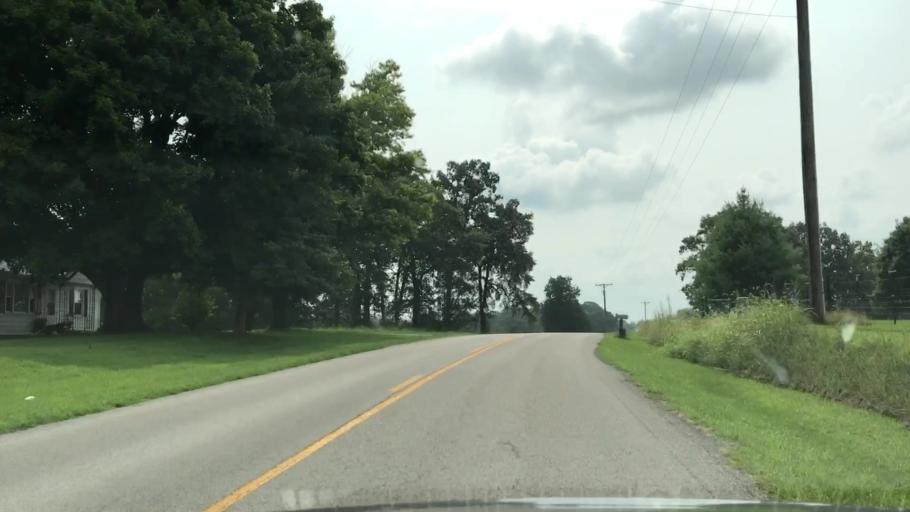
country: US
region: Kentucky
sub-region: Edmonson County
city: Brownsville
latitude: 37.1404
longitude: -86.1814
